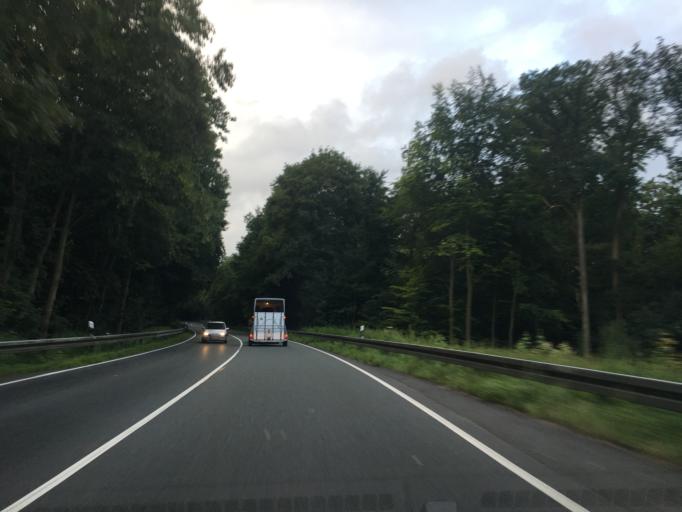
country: DE
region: North Rhine-Westphalia
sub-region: Regierungsbezirk Munster
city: Muenster
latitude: 51.9696
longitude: 7.6726
